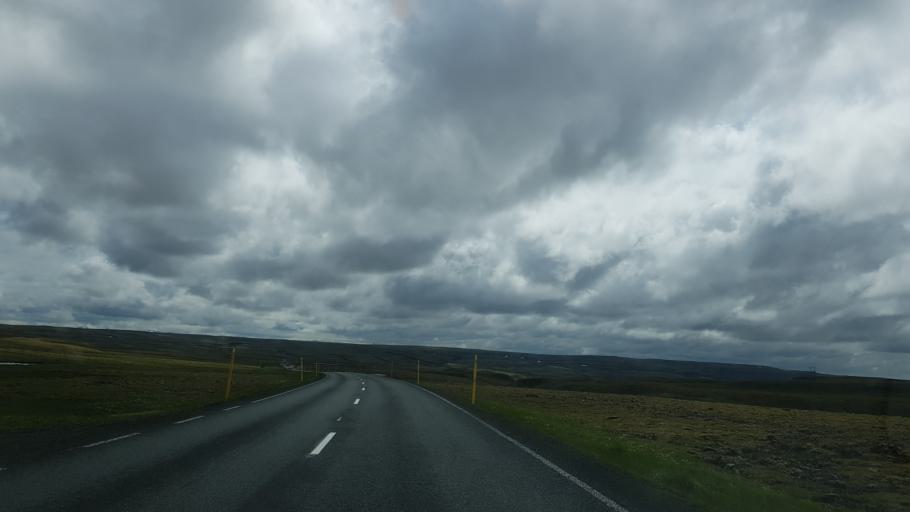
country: IS
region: West
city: Borgarnes
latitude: 64.9586
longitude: -21.0607
